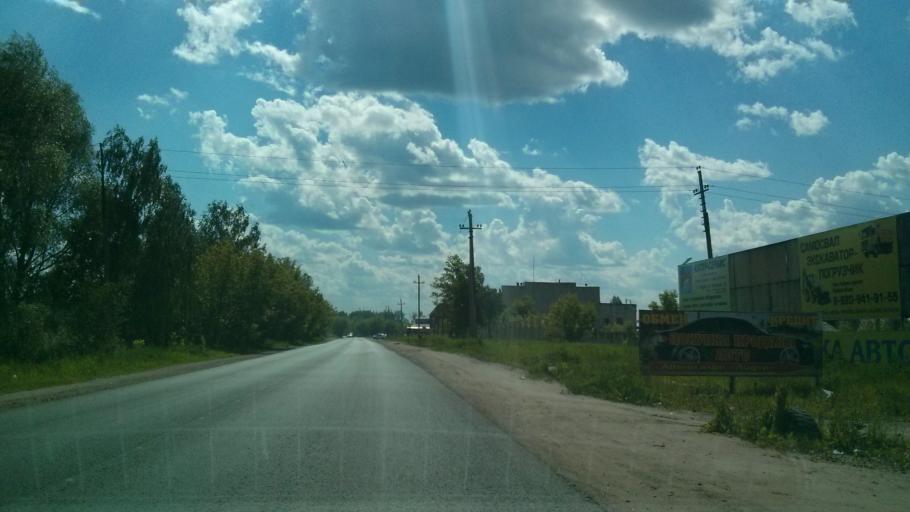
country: RU
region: Vladimir
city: Murom
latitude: 55.5553
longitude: 42.0082
